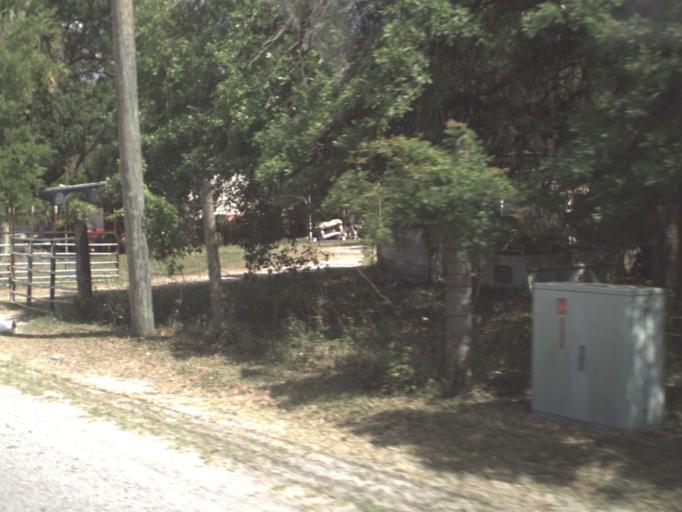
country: US
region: Florida
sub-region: Lake County
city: Mount Dora
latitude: 28.8005
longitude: -81.6136
